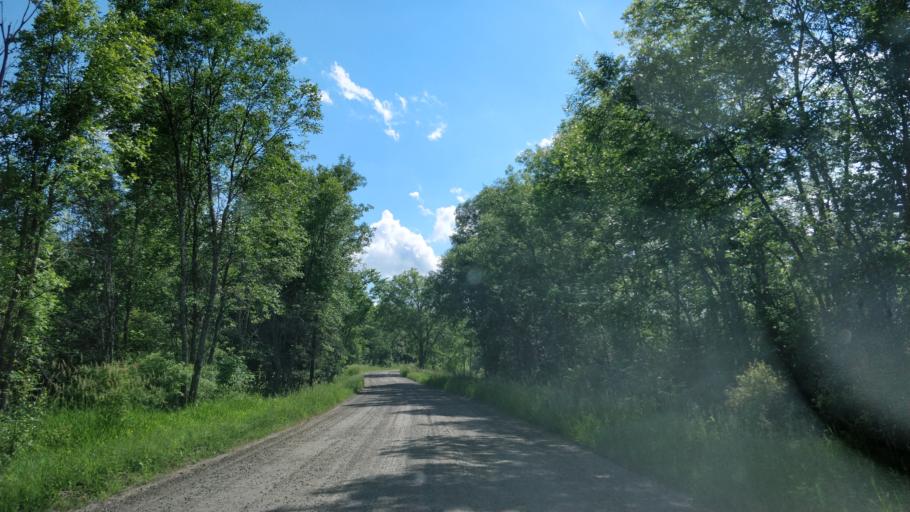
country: CA
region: Ontario
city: Perth
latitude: 44.7259
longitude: -76.5105
